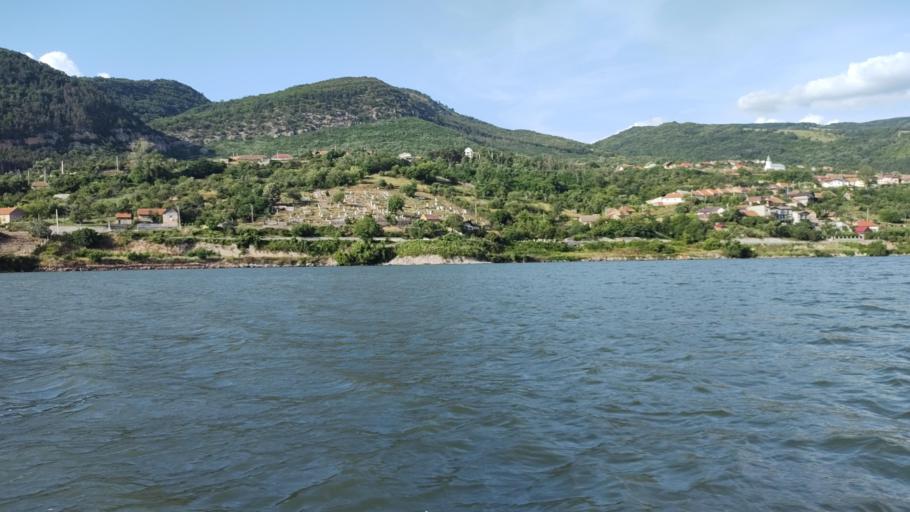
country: RO
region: Mehedinti
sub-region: Comuna Svinita
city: Svinita
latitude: 44.4963
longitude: 22.0955
